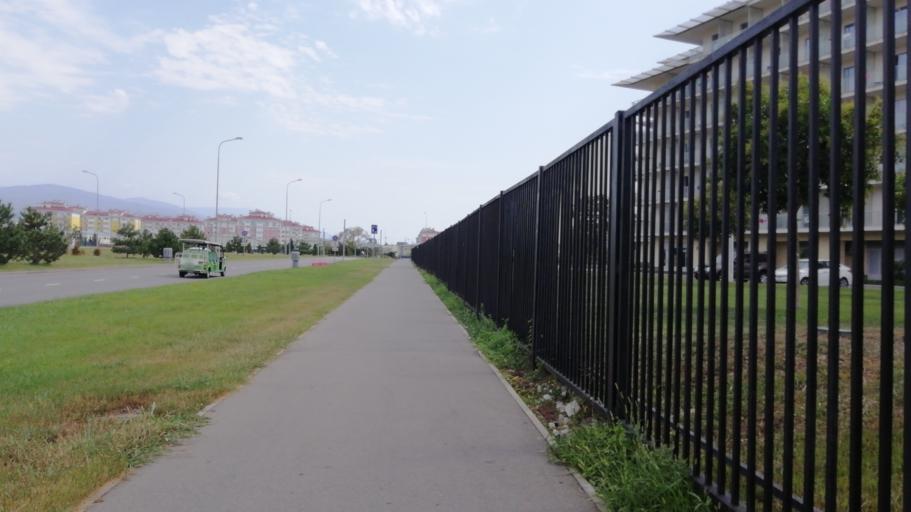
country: RU
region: Krasnodarskiy
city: Adler
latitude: 43.4043
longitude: 39.9777
